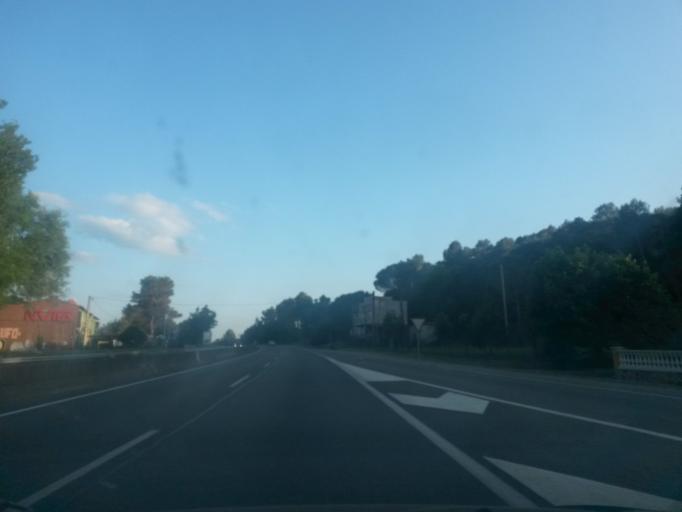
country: ES
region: Catalonia
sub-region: Provincia de Girona
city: Palol de Revardit
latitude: 42.0632
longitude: 2.8123
